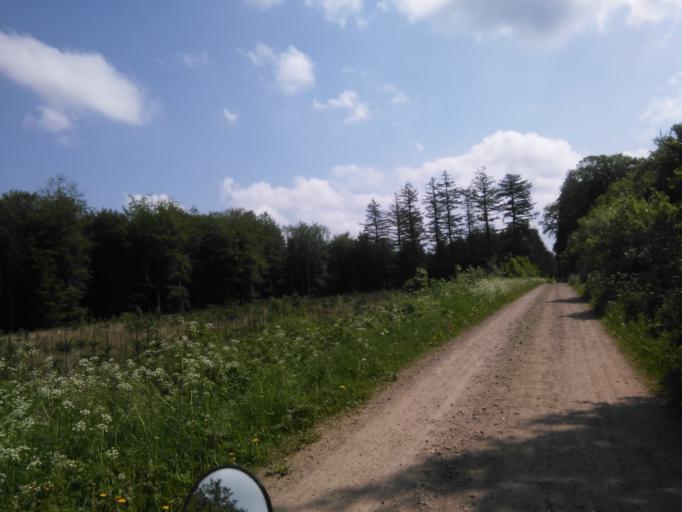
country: DK
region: Central Jutland
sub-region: Favrskov Kommune
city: Hinnerup
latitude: 56.2646
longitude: 10.0403
